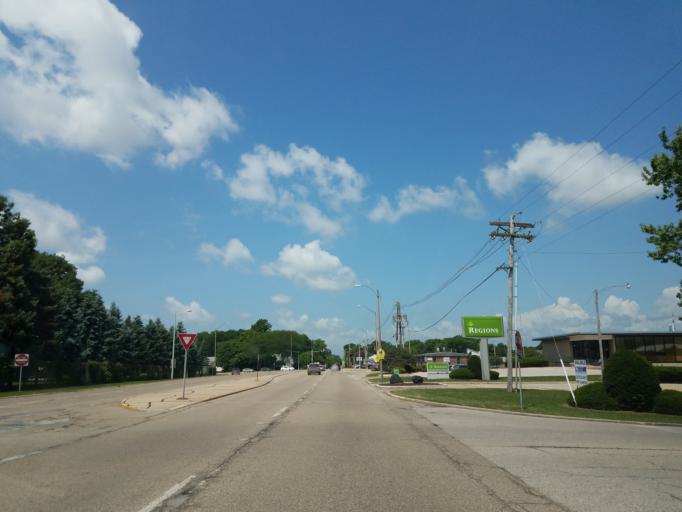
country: US
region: Illinois
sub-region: McLean County
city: Bloomington
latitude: 40.4885
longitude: -88.9679
